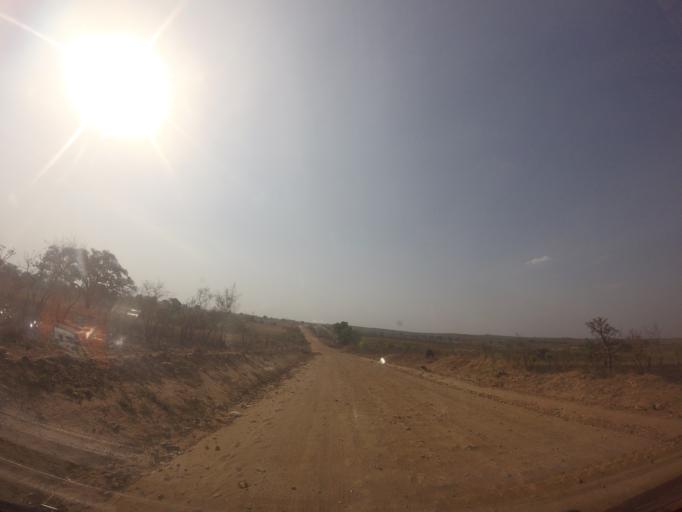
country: UG
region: Northern Region
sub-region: Maracha District
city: Maracha
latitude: 3.1030
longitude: 31.2118
